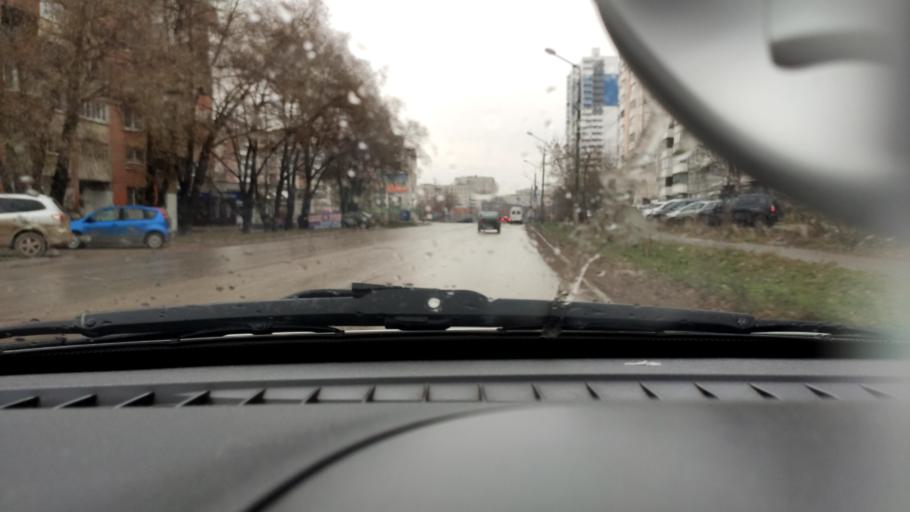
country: RU
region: Perm
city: Perm
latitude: 57.9686
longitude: 56.2257
